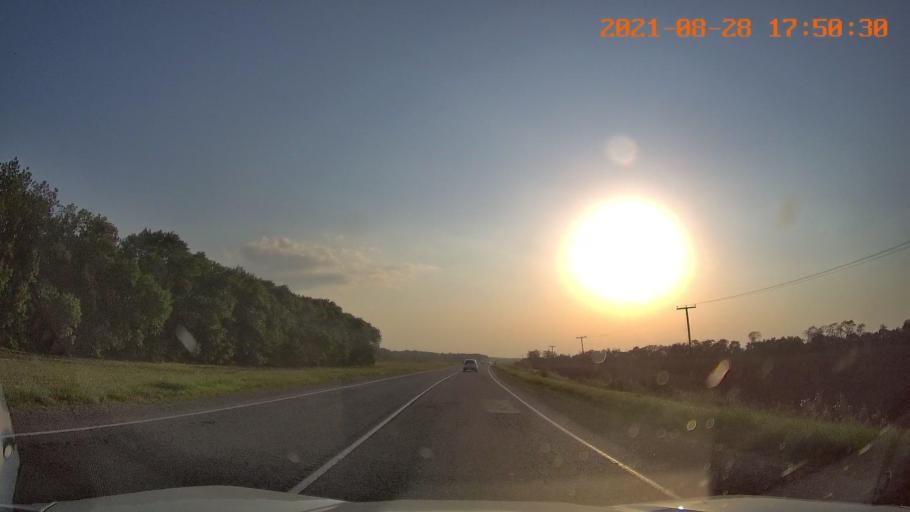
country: RU
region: Krasnodarskiy
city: Konstantinovskaya
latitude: 44.9472
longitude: 40.8136
